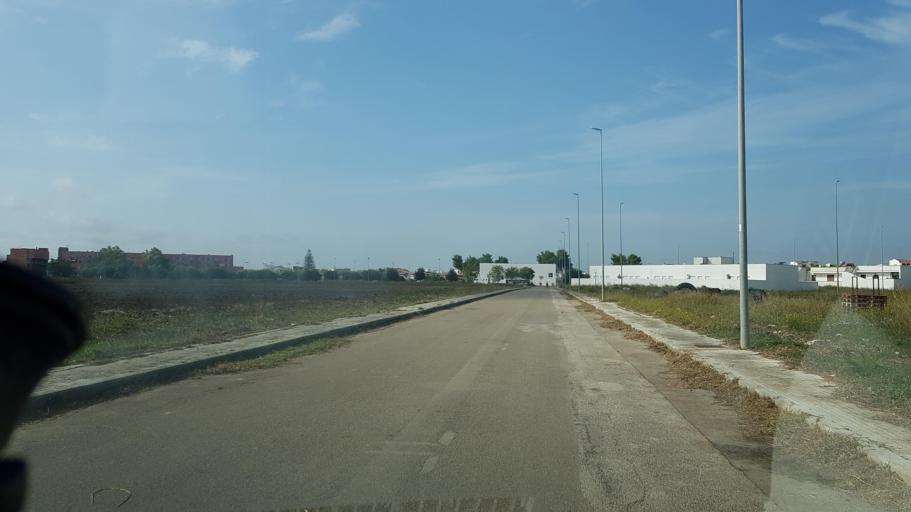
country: IT
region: Apulia
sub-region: Provincia di Brindisi
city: San Donaci
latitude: 40.4471
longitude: 17.9312
